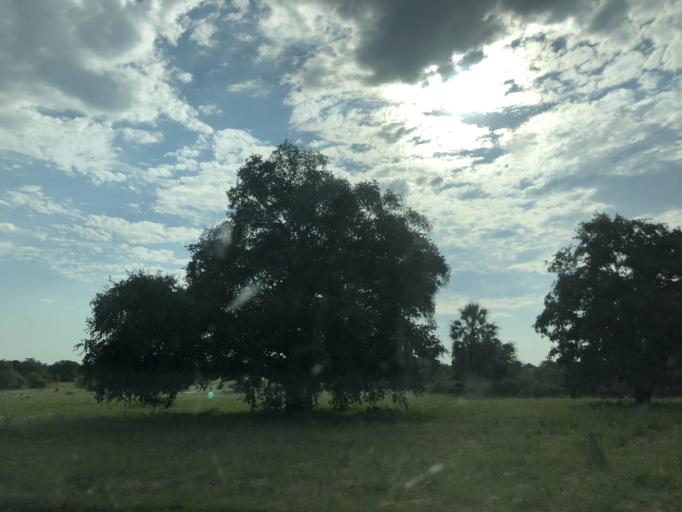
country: AO
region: Cunene
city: Ondjiva
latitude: -17.0754
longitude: 15.6804
